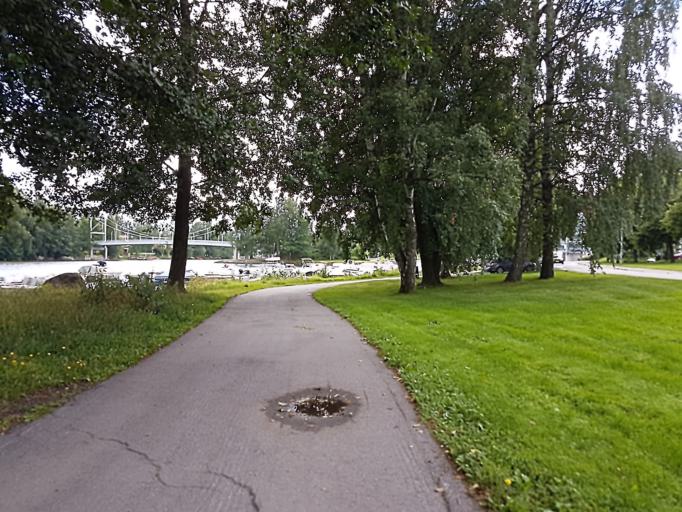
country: FI
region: Pirkanmaa
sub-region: Etelae-Pirkanmaa
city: Valkeakoski
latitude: 61.2690
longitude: 24.0365
